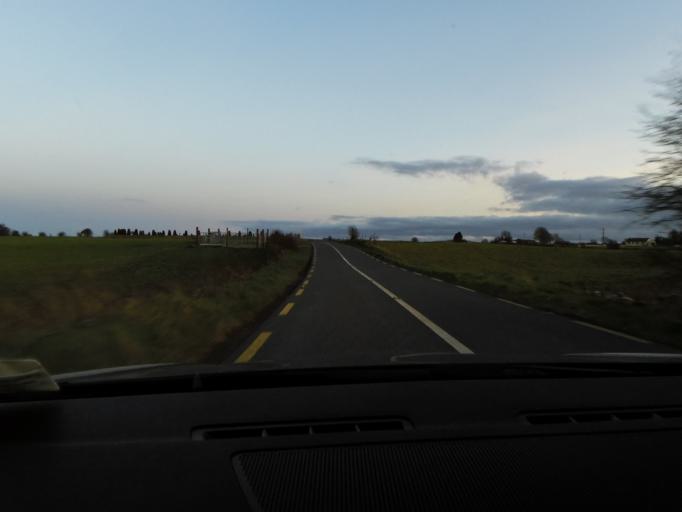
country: IE
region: Connaught
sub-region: Roscommon
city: Boyle
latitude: 53.8839
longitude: -8.2489
